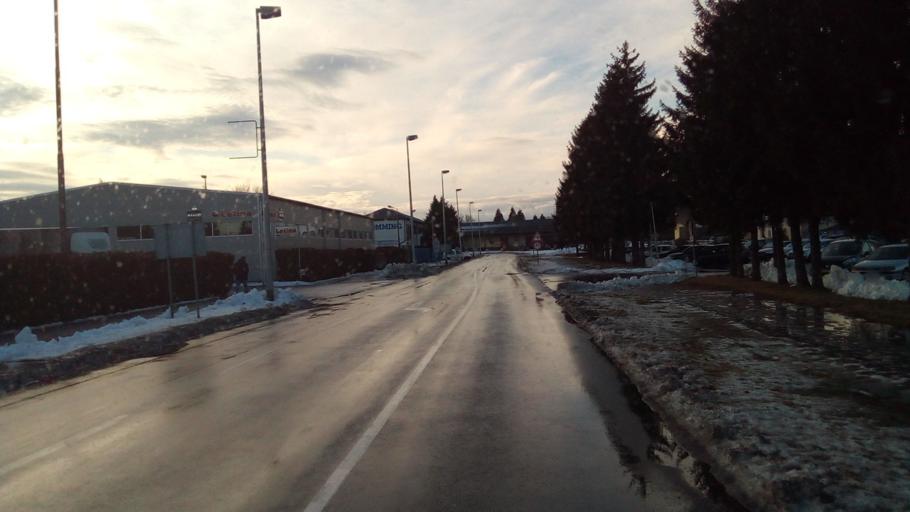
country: HR
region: Medimurska
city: Cakovec
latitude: 46.3870
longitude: 16.4198
